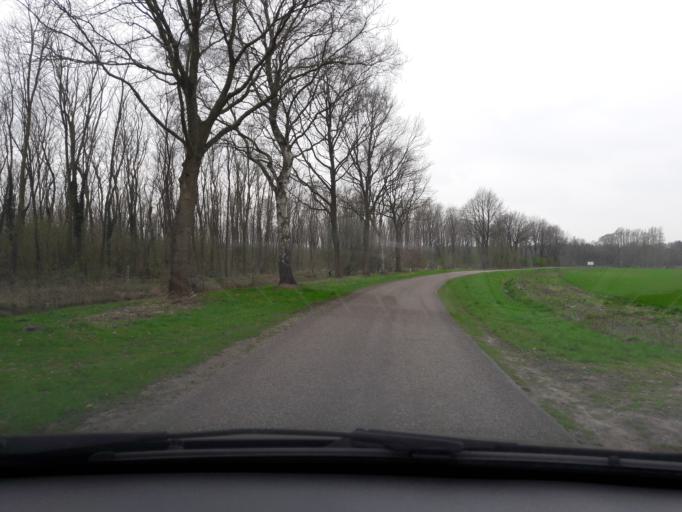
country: NL
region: Drenthe
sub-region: Gemeente Borger-Odoorn
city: Borger
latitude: 52.9237
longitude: 6.6820
